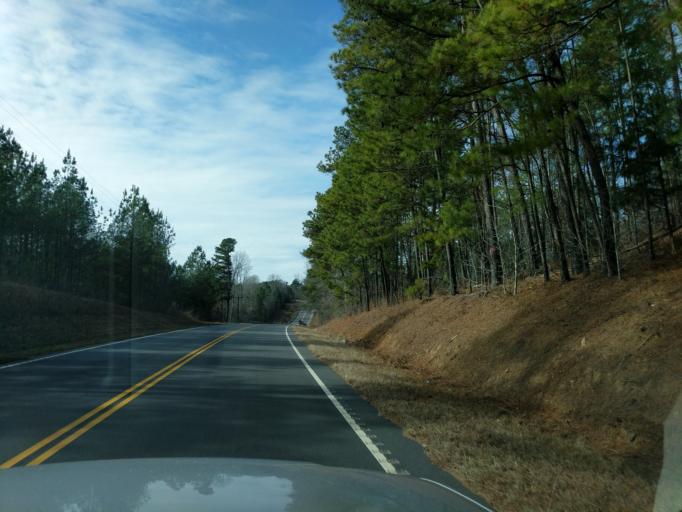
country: US
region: South Carolina
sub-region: Edgefield County
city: Edgefield
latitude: 33.9384
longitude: -81.9368
